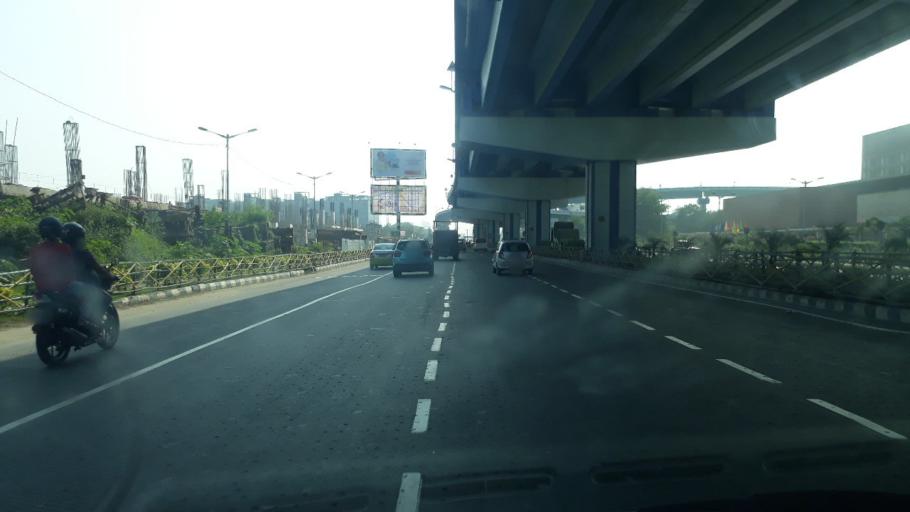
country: IN
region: West Bengal
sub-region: Kolkata
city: Kolkata
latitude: 22.5453
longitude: 88.3992
